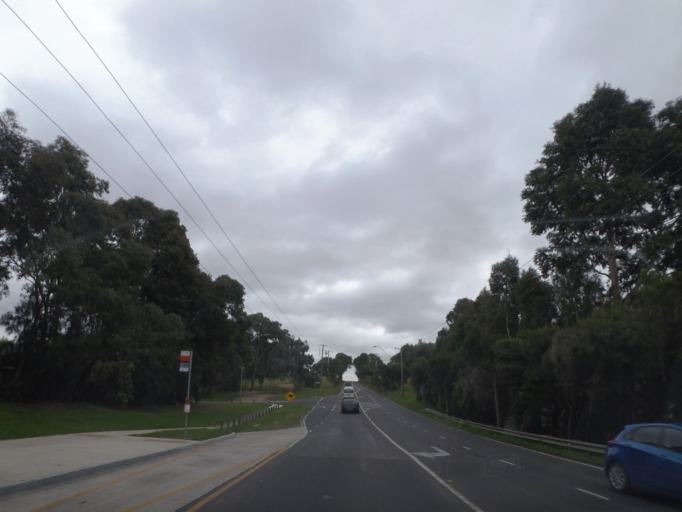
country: AU
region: Victoria
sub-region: Nillumbik
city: Eltham North
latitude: -37.6862
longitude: 145.1430
